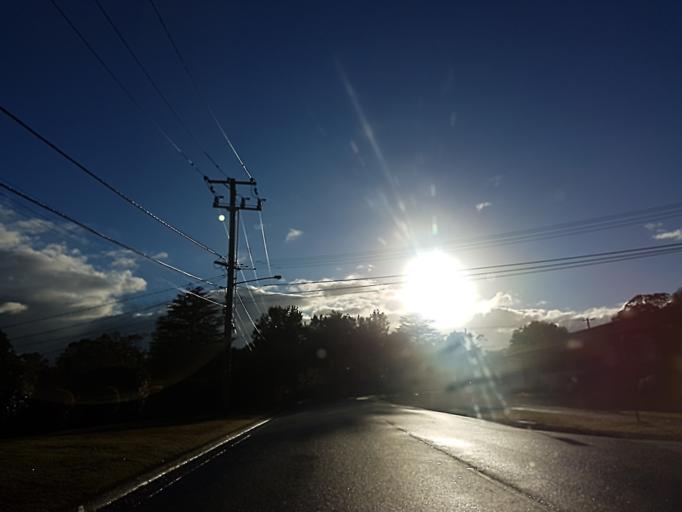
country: AU
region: New South Wales
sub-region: Warringah
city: Davidson
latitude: -33.7348
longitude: 151.2126
